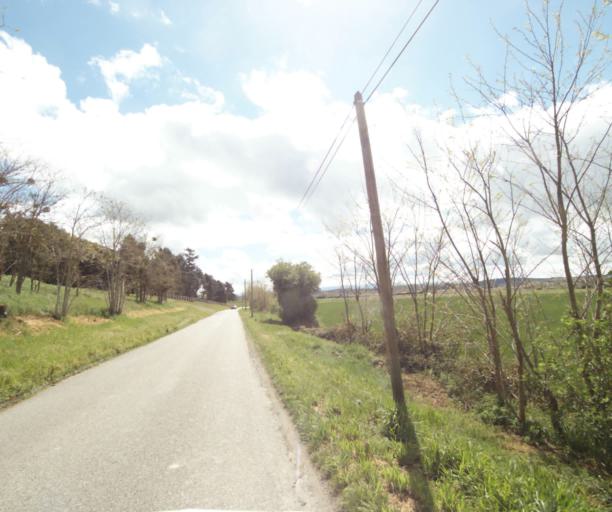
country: FR
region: Midi-Pyrenees
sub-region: Departement de l'Ariege
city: Saverdun
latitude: 43.2465
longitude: 1.5896
